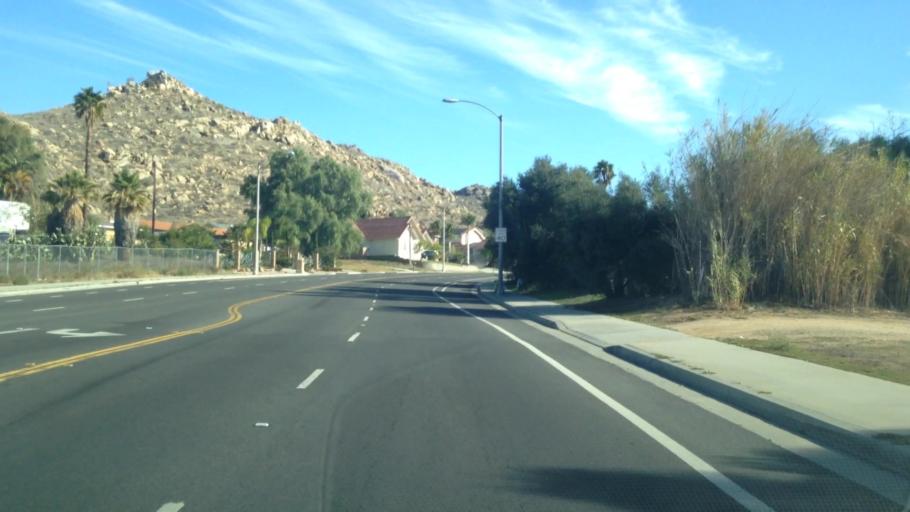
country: US
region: California
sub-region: Riverside County
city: Pedley
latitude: 33.9206
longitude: -117.4681
